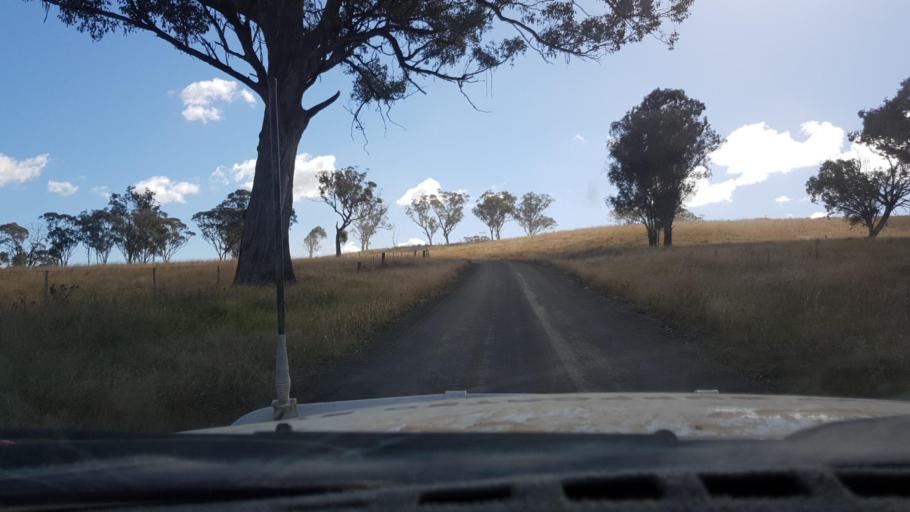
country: AU
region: New South Wales
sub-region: Narrabri
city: Blair Athol
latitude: -30.5515
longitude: 150.4619
